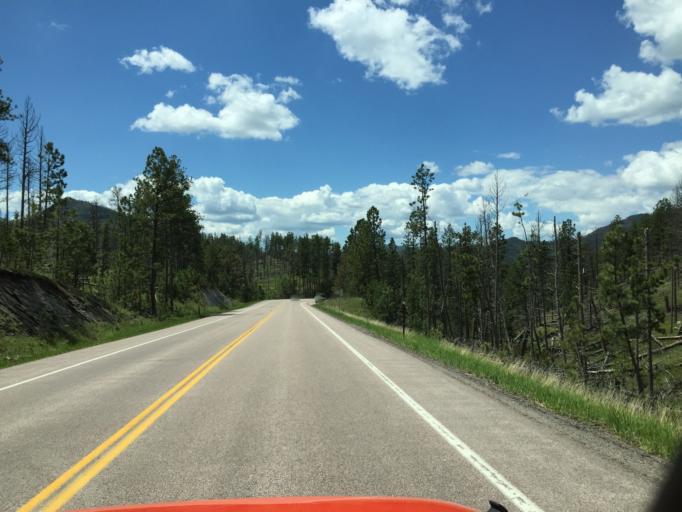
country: US
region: South Dakota
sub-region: Custer County
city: Custer
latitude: 43.8962
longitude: -103.5814
